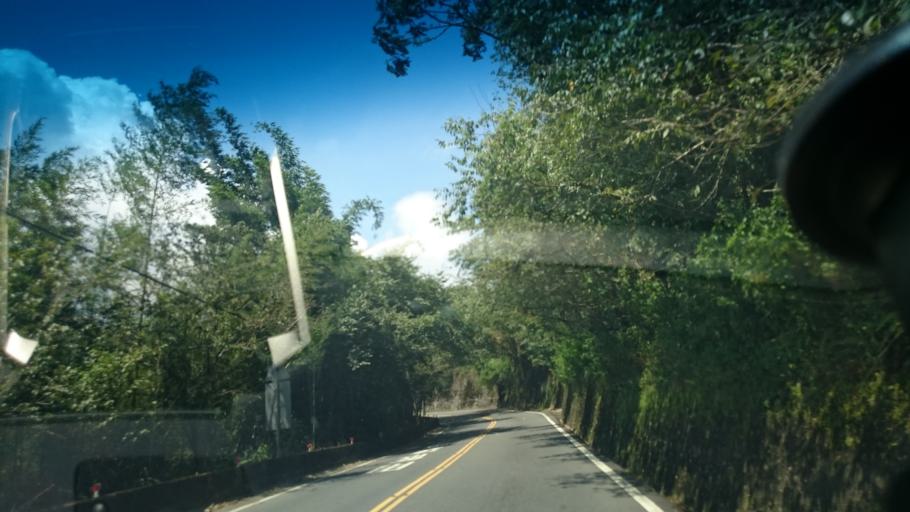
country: TW
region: Taiwan
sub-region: Nantou
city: Puli
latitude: 24.0165
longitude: 121.1289
